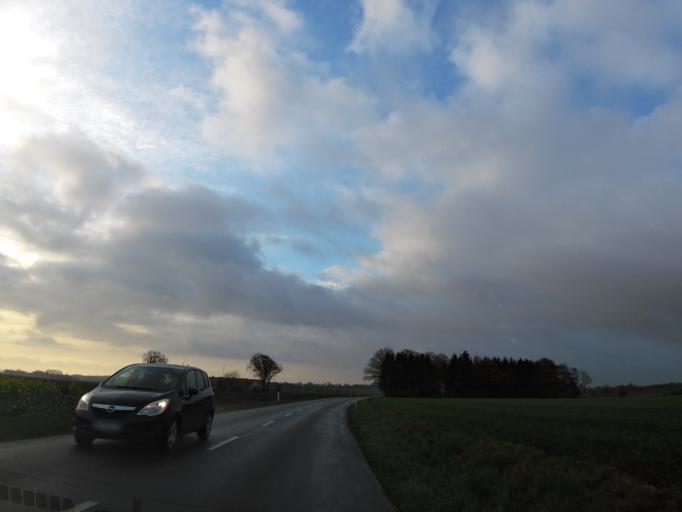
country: DK
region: Central Jutland
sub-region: Odder Kommune
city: Odder
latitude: 55.9510
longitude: 10.2368
